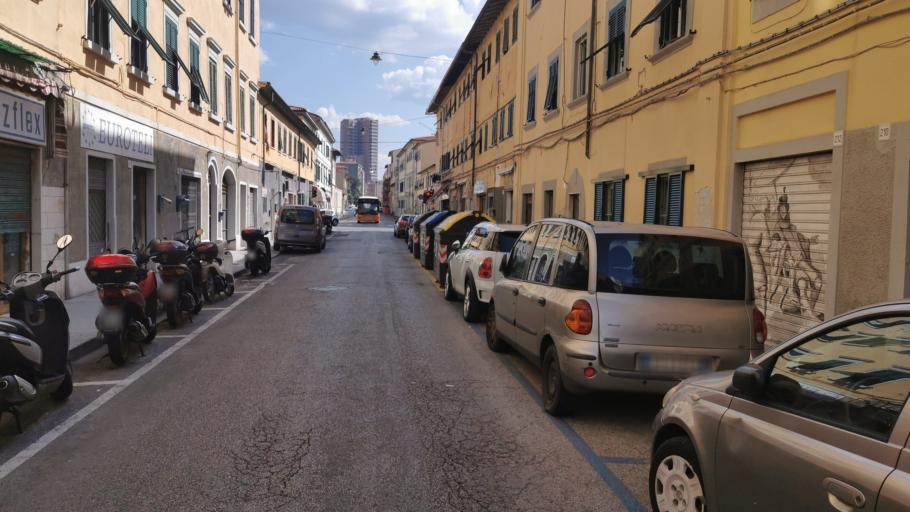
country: IT
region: Tuscany
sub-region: Provincia di Livorno
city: Livorno
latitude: 43.5435
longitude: 10.3072
